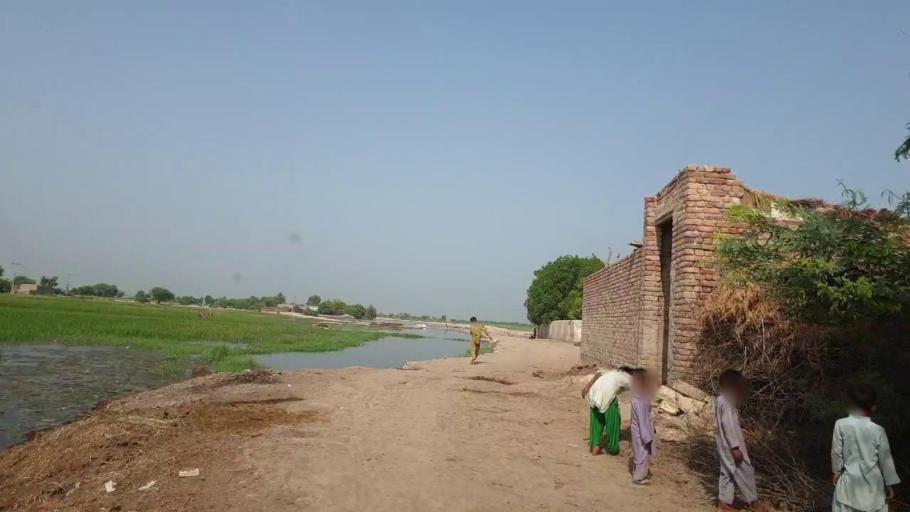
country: PK
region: Sindh
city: Bagarji
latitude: 27.8064
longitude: 68.7441
